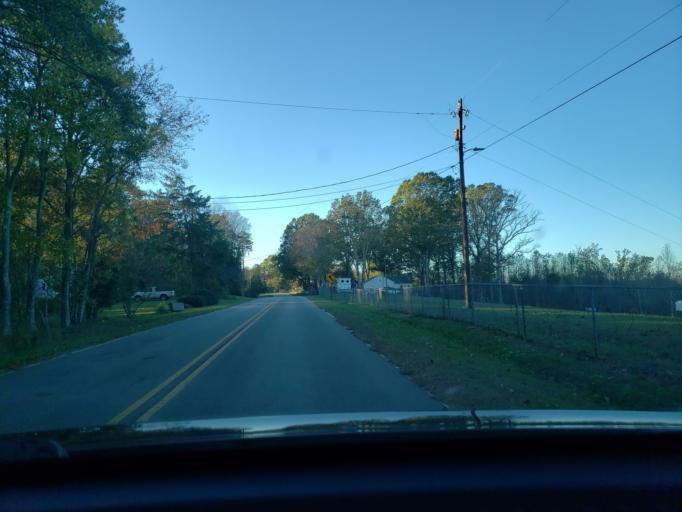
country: US
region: North Carolina
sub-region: Forsyth County
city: Walkertown
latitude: 36.2222
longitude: -80.1891
